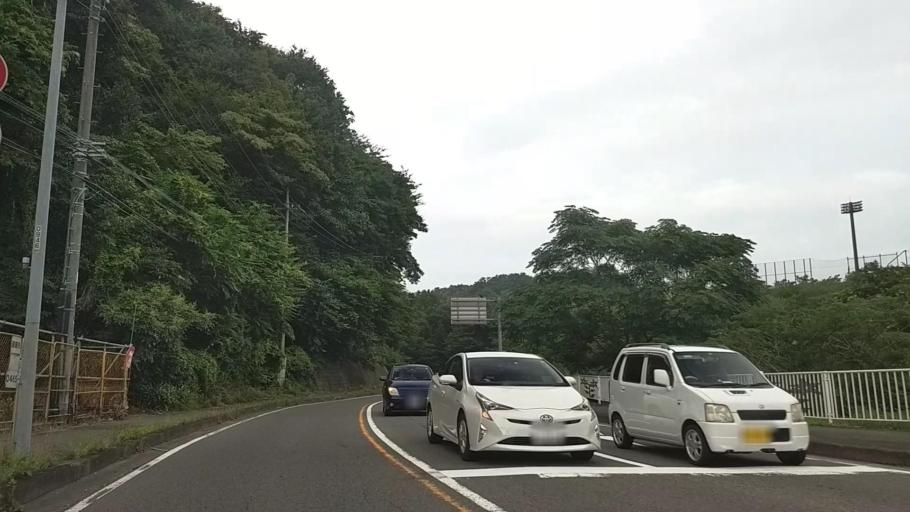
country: JP
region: Kanagawa
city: Hadano
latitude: 35.3412
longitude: 139.2220
